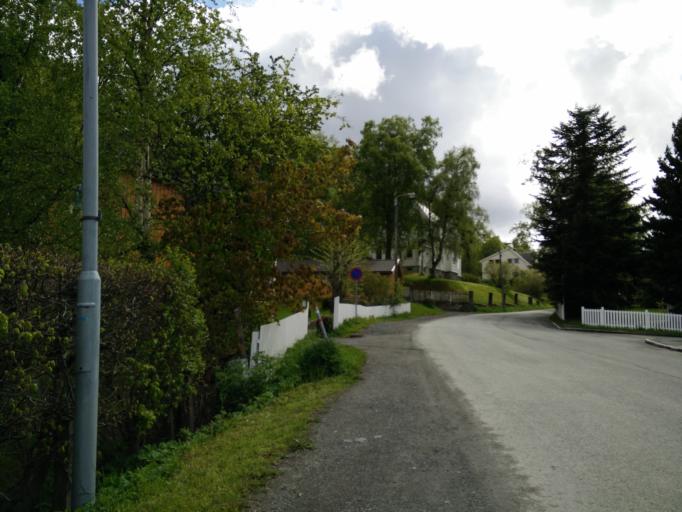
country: NO
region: Sor-Trondelag
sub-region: Trondheim
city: Trondheim
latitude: 63.4076
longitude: 10.4041
